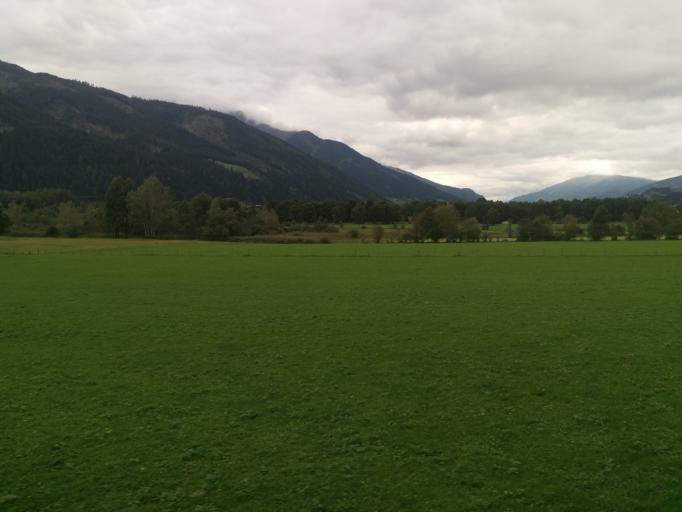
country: AT
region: Salzburg
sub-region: Politischer Bezirk Zell am See
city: Uttendorf
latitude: 47.2854
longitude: 12.5441
